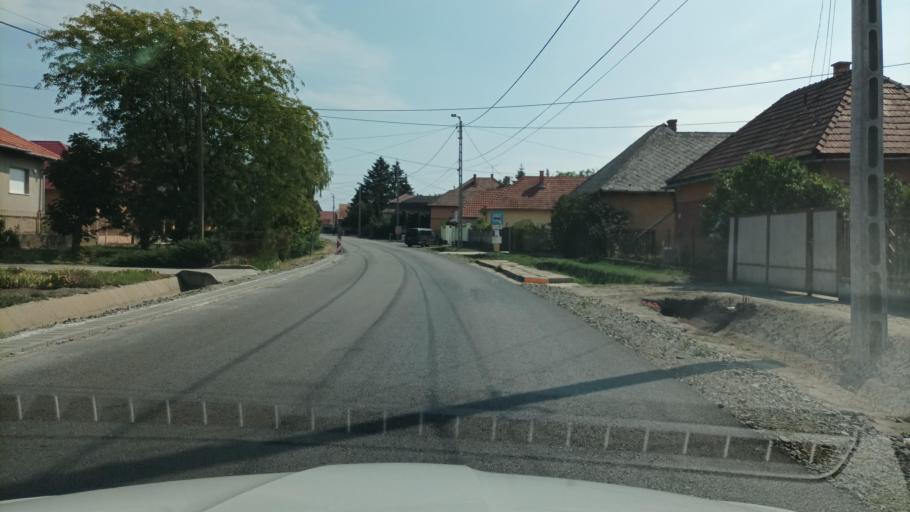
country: HU
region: Pest
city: Tura
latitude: 47.6097
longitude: 19.5902
